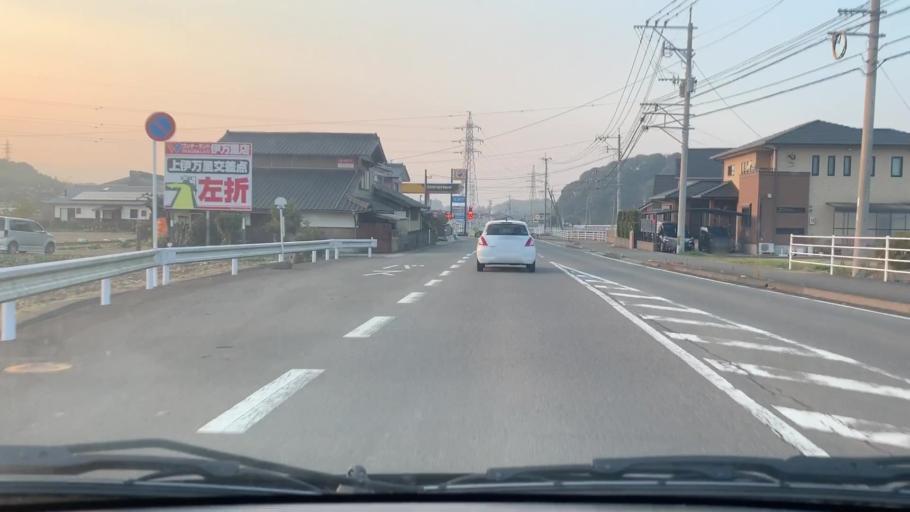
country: JP
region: Saga Prefecture
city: Imaricho-ko
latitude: 33.2690
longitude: 129.8974
